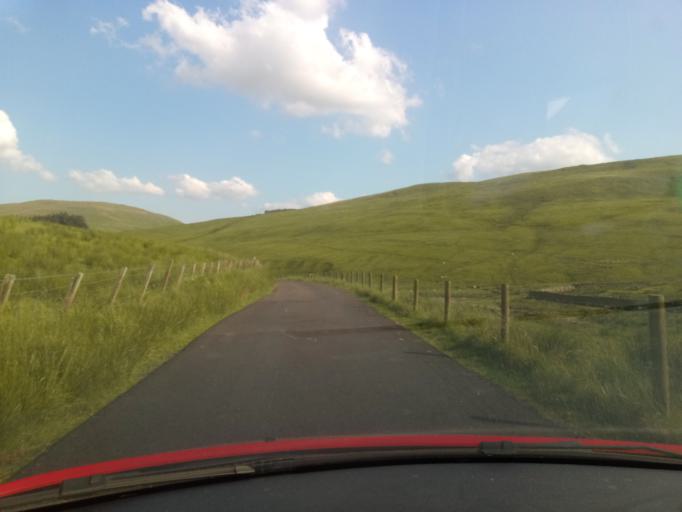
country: GB
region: Scotland
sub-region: The Scottish Borders
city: Innerleithen
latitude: 55.4565
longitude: -3.1118
